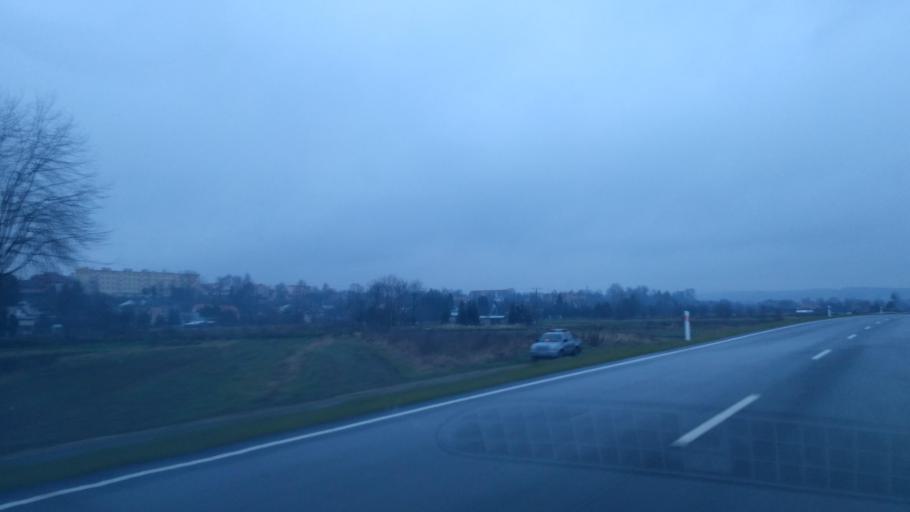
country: PL
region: Subcarpathian Voivodeship
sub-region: Powiat rzeszowski
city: Dynow
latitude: 49.8111
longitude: 22.2405
